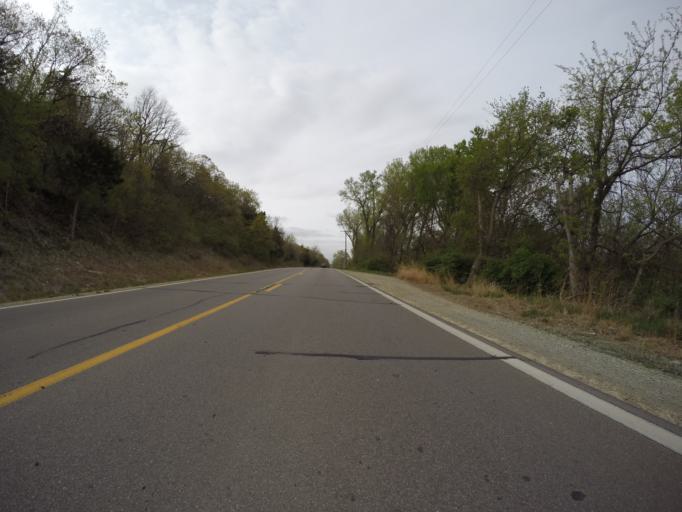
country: US
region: Kansas
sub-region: Riley County
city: Manhattan
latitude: 39.1591
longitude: -96.5566
